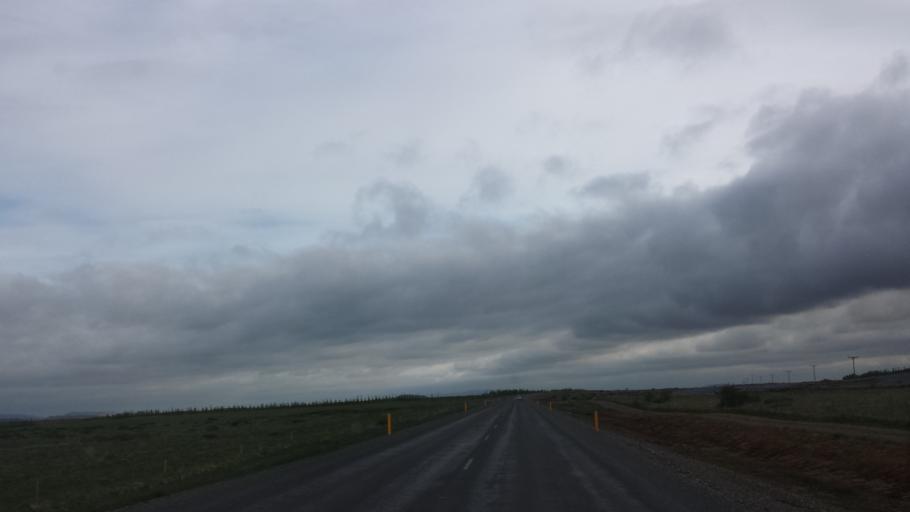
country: IS
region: South
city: Selfoss
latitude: 64.2804
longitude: -20.3458
